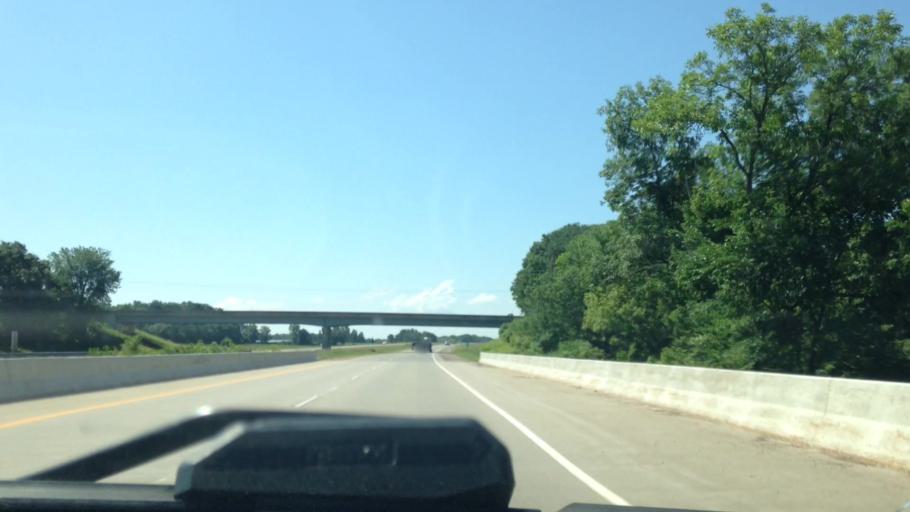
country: US
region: Wisconsin
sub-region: Barron County
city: Cameron
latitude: 45.4462
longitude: -91.7598
